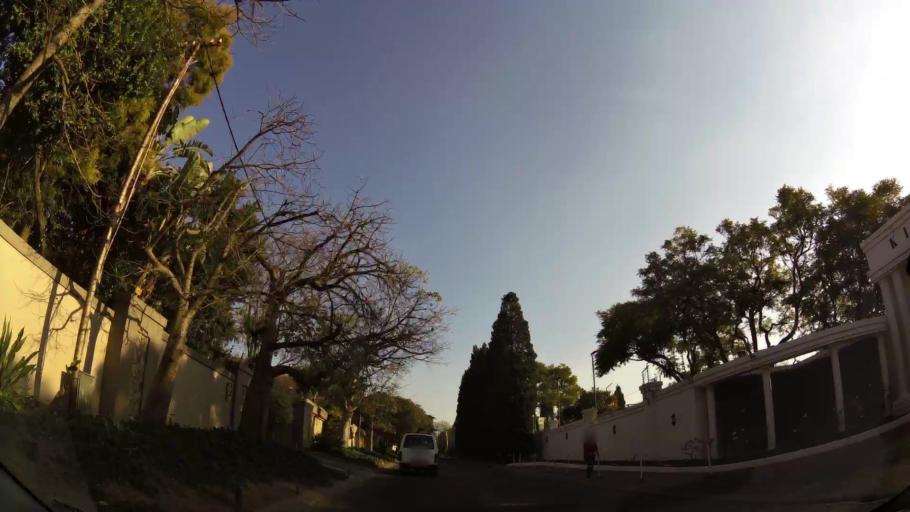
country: ZA
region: Gauteng
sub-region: City of Johannesburg Metropolitan Municipality
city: Diepsloot
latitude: -26.0580
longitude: 27.9948
